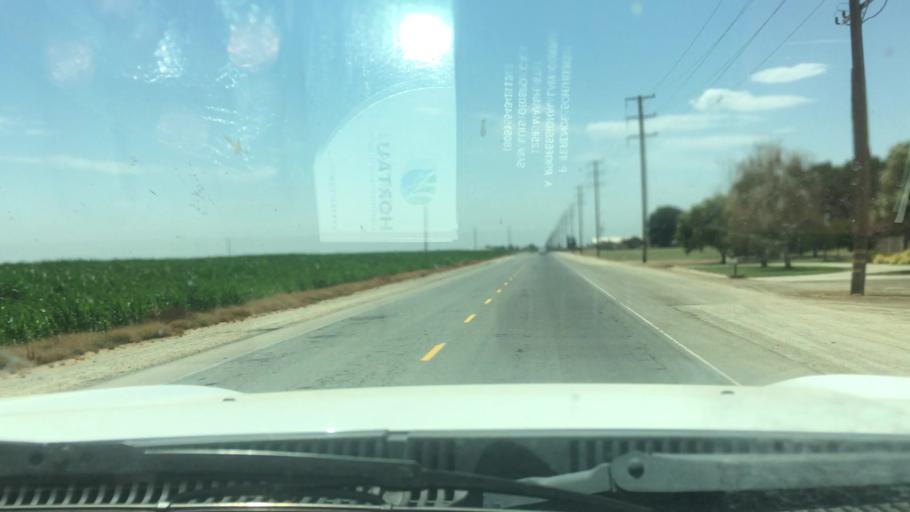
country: US
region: California
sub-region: Tulare County
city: Tipton
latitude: 36.0657
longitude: -119.2638
